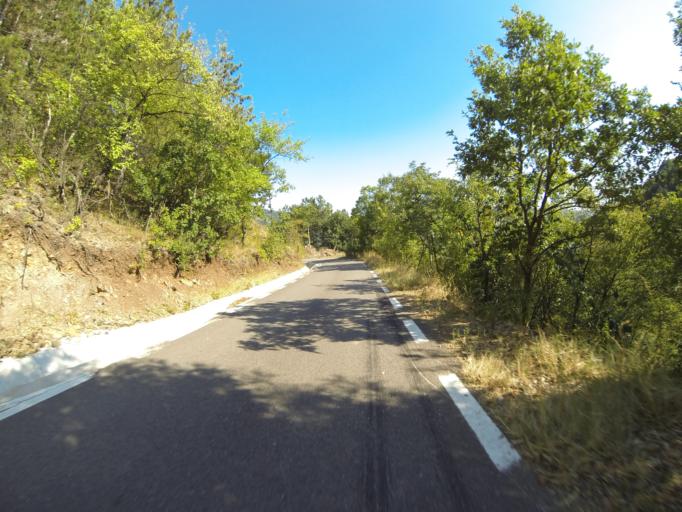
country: RO
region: Mehedinti
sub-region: Comuna Dubova
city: Dubova
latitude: 44.5395
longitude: 22.2079
